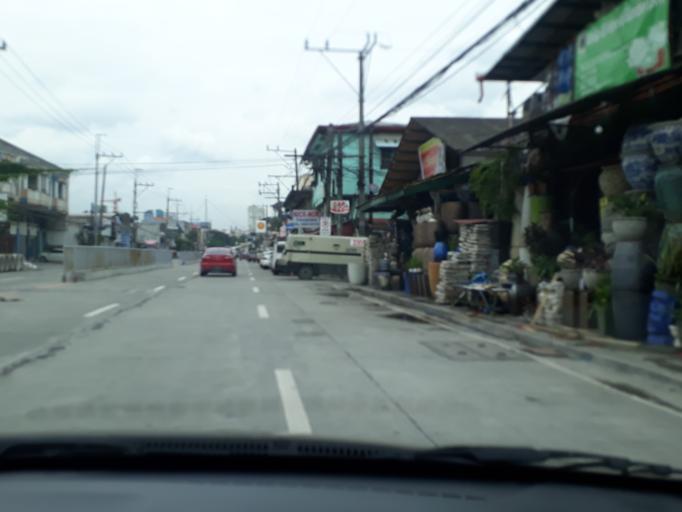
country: PH
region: Metro Manila
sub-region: Mandaluyong
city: Mandaluyong City
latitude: 14.5741
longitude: 121.0305
